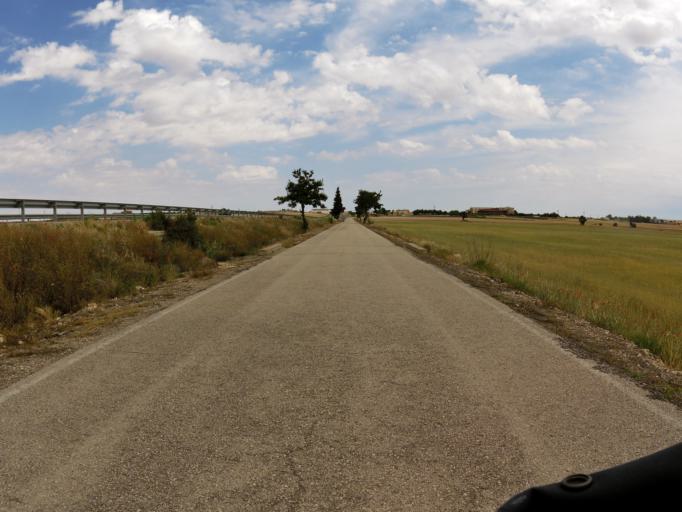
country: ES
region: Castille-La Mancha
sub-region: Provincia de Albacete
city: Valdeganga
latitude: 39.1217
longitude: -1.6831
